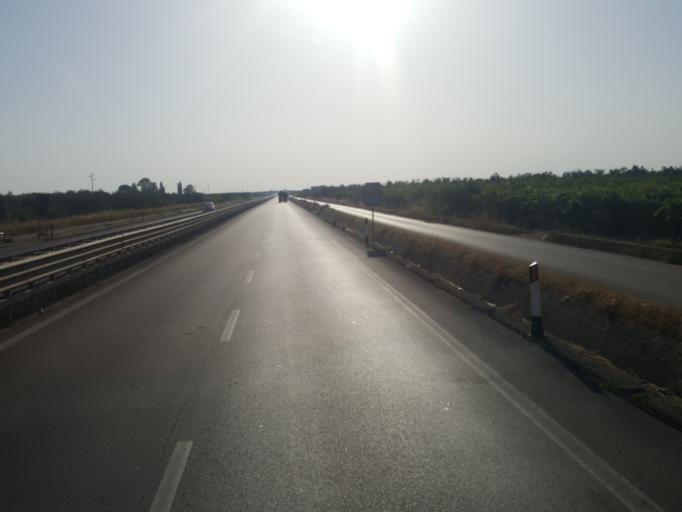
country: IT
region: Apulia
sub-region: Provincia di Barletta - Andria - Trani
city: San Ferdinando di Puglia
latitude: 41.3142
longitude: 16.1090
